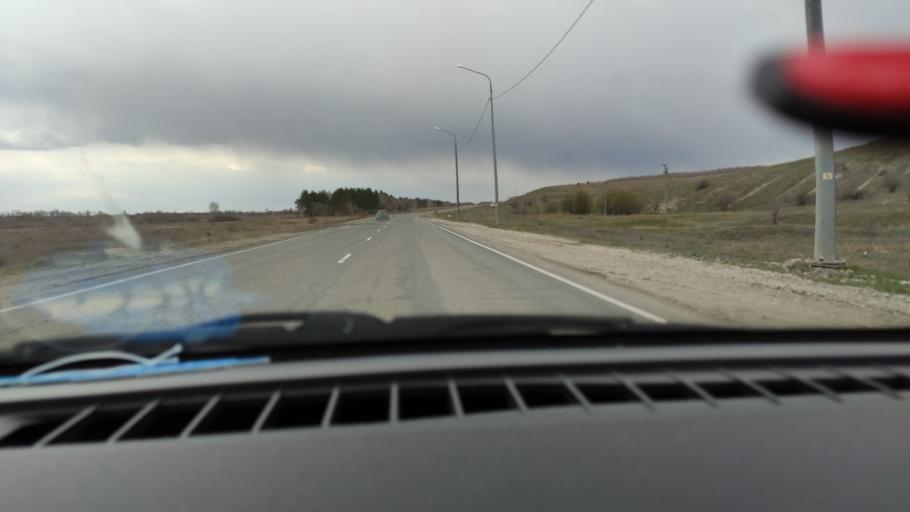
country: RU
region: Saratov
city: Sinodskoye
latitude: 52.0769
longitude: 46.7889
